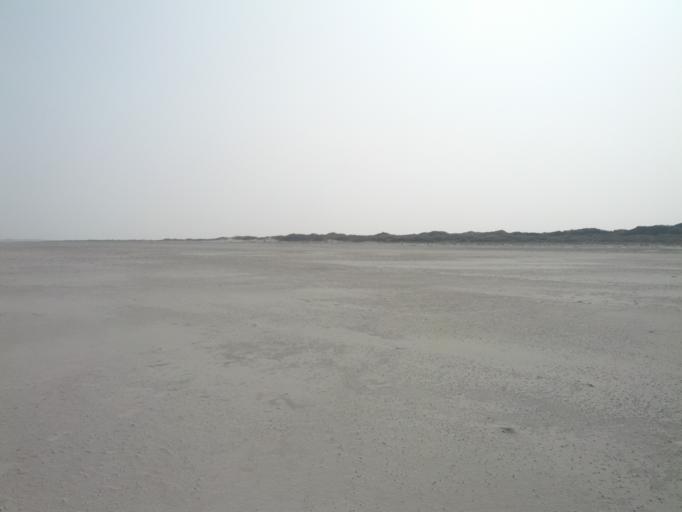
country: DE
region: Lower Saxony
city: Spiekeroog
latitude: 53.7587
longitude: 7.5895
